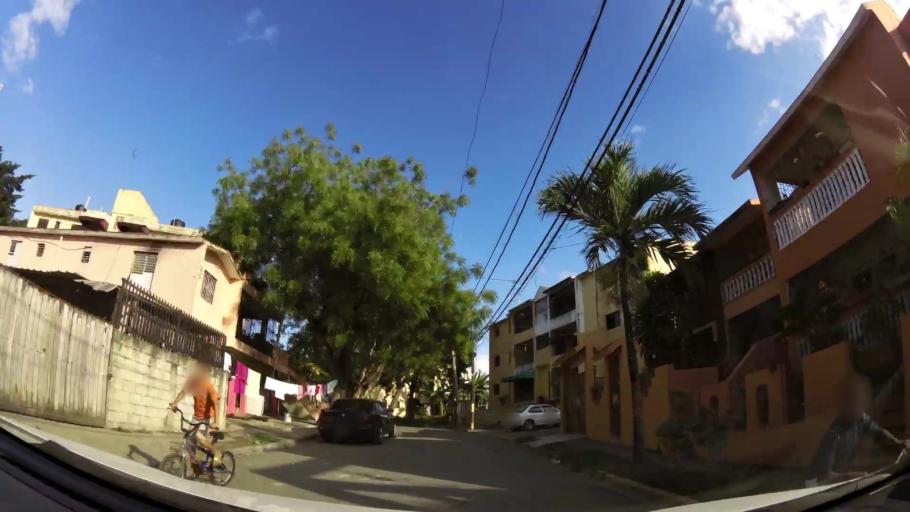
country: DO
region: Nacional
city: Ensanche Luperon
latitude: 18.5580
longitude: -69.8948
